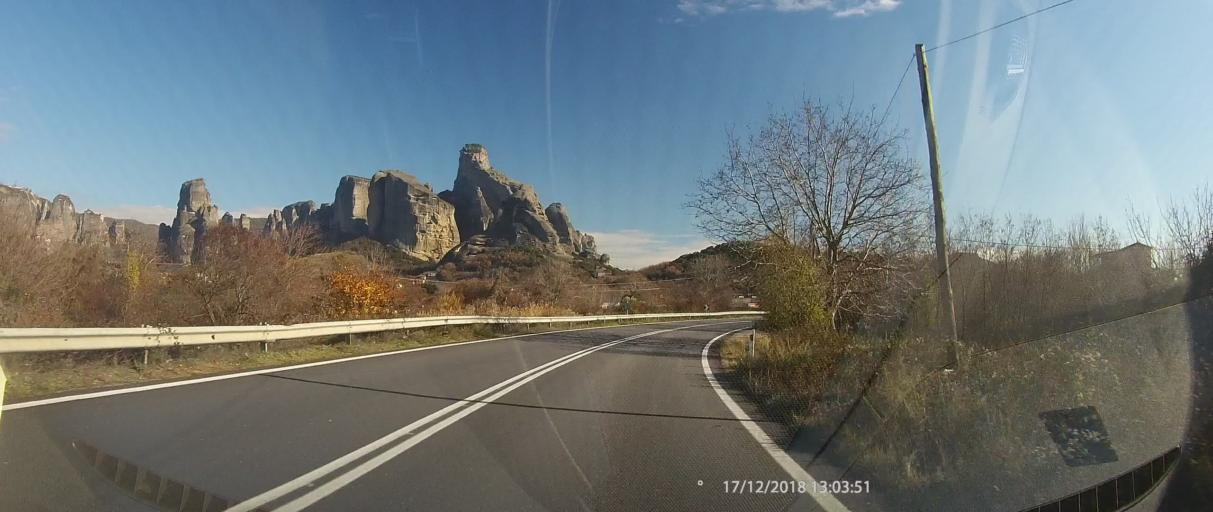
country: GR
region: Thessaly
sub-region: Trikala
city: Kastraki
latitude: 39.7105
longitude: 21.6049
